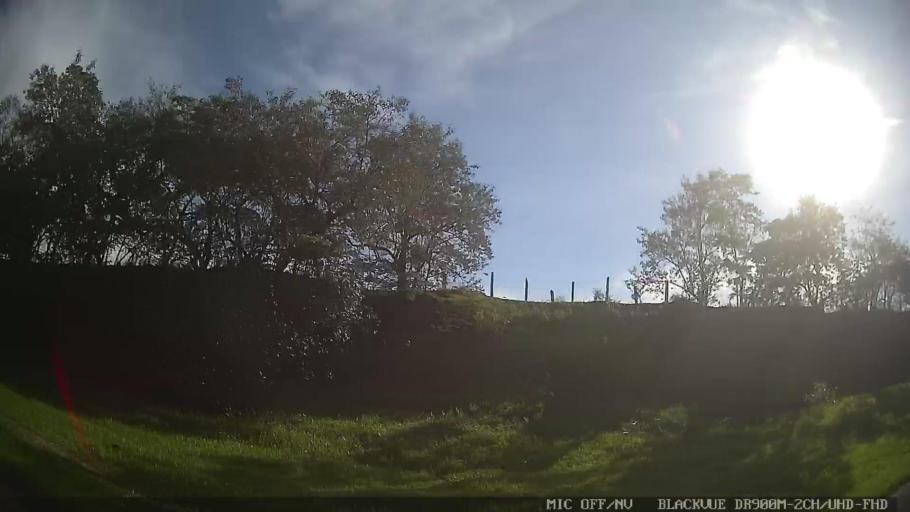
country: BR
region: Sao Paulo
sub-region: Tiete
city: Tiete
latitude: -23.1102
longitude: -47.7483
